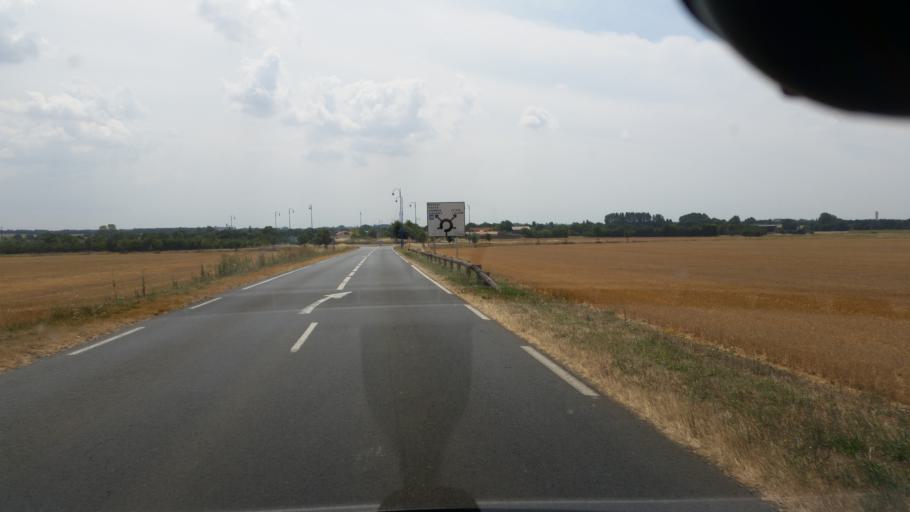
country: FR
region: Poitou-Charentes
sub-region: Departement de la Charente-Maritime
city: Saint-Jean-de-Liversay
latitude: 46.1973
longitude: -0.8696
